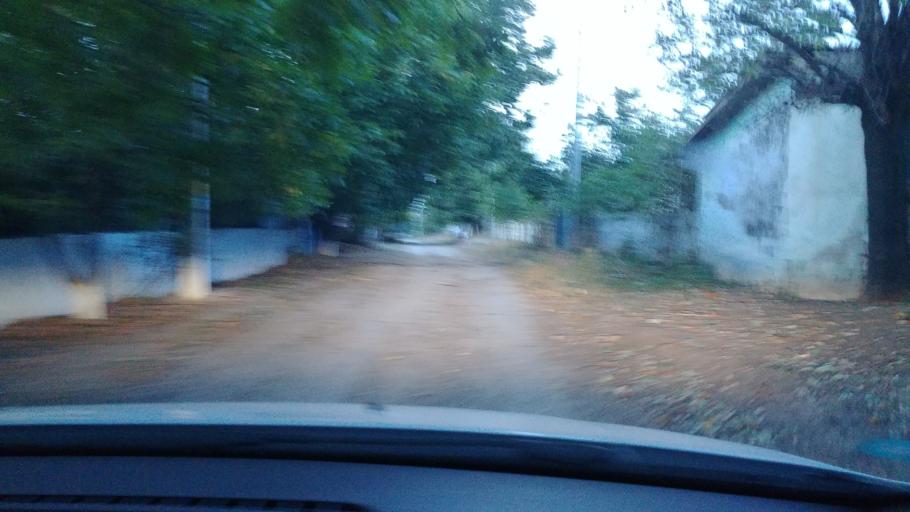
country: MD
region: Rezina
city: Saharna
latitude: 47.6767
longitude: 28.9606
